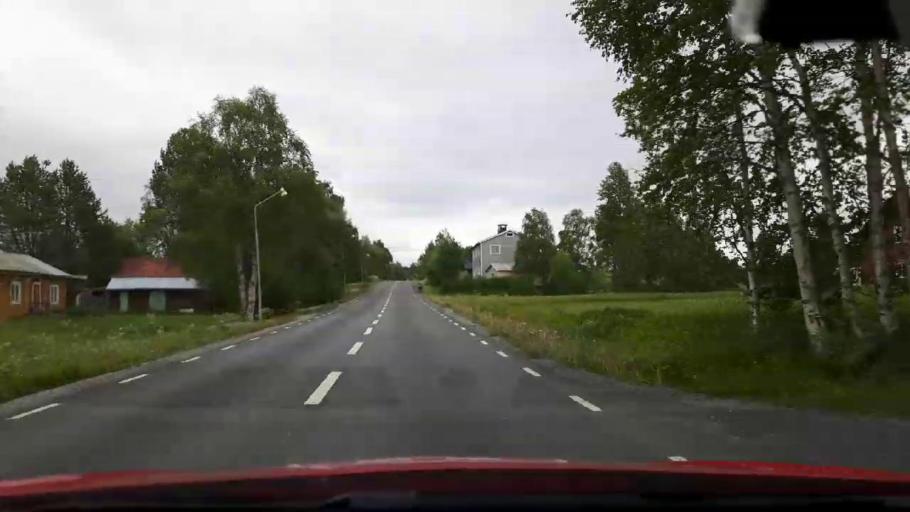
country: SE
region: Jaemtland
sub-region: OEstersunds Kommun
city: Lit
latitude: 63.7429
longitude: 14.8479
